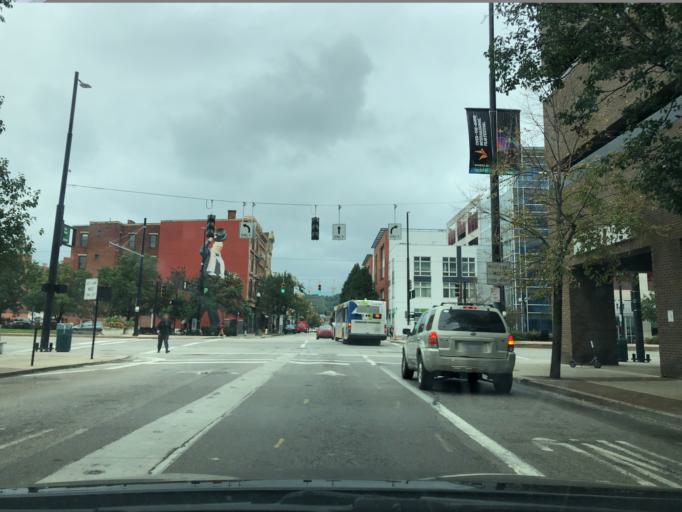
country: US
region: Kentucky
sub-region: Kenton County
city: Covington
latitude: 39.1068
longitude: -84.5144
